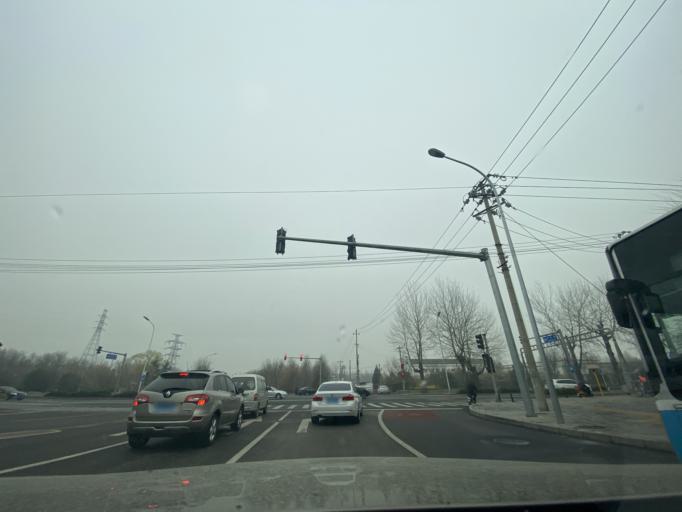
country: CN
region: Beijing
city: Sijiqing
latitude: 39.9715
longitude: 116.2402
